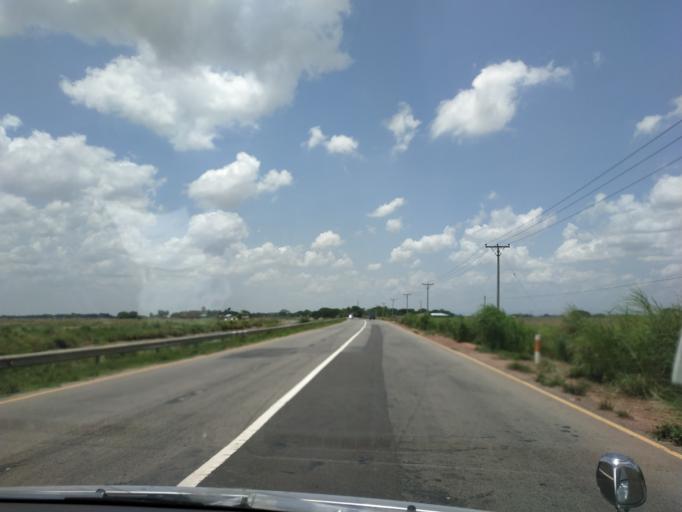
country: MM
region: Bago
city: Thanatpin
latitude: 17.5016
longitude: 96.7057
